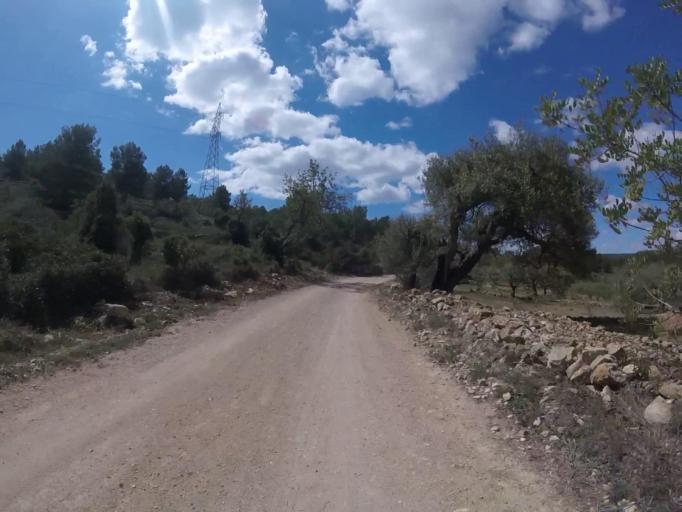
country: ES
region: Valencia
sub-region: Provincia de Castello
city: Santa Magdalena de Pulpis
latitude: 40.3245
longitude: 0.3508
